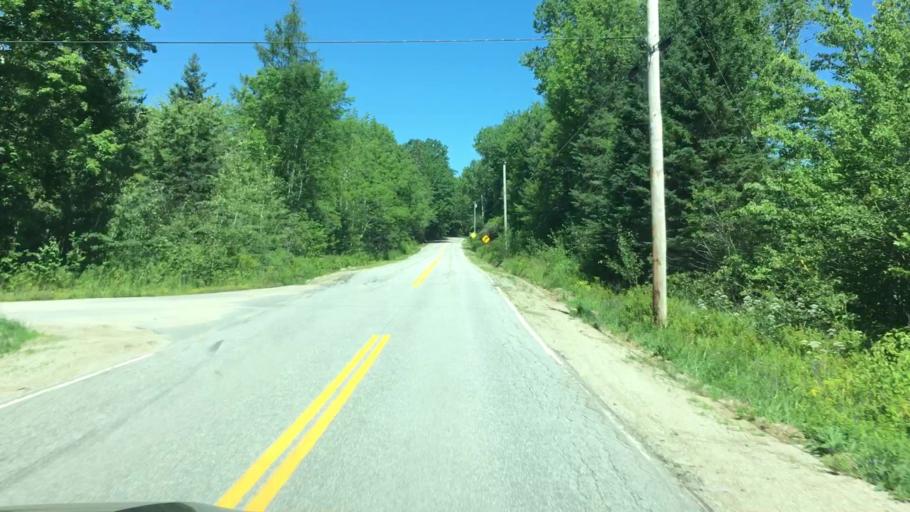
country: US
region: Maine
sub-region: Hancock County
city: Penobscot
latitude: 44.4259
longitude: -68.7104
